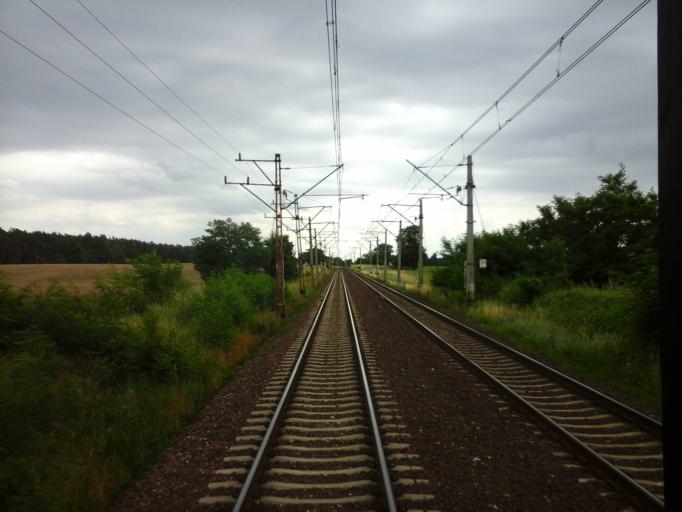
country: PL
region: West Pomeranian Voivodeship
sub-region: Powiat stargardzki
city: Dolice
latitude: 53.2134
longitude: 15.1631
